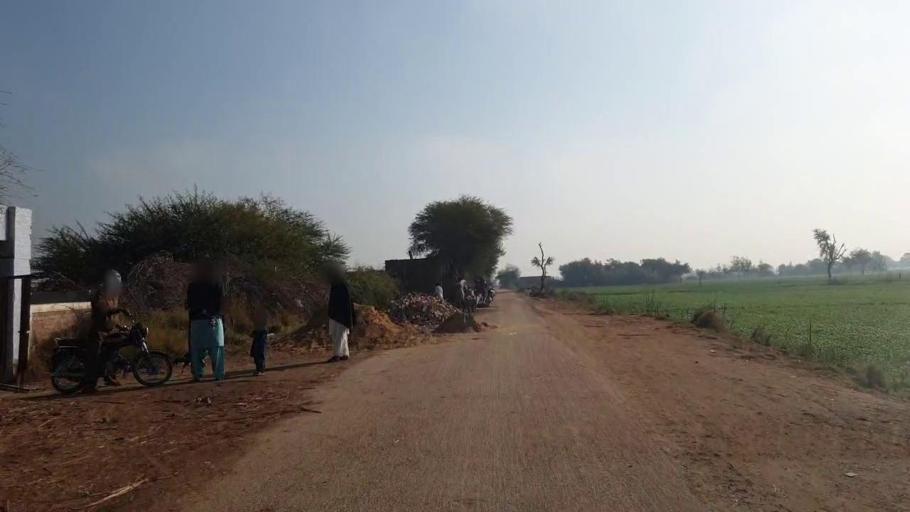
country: PK
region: Sindh
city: Shahdadpur
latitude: 26.0003
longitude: 68.6035
